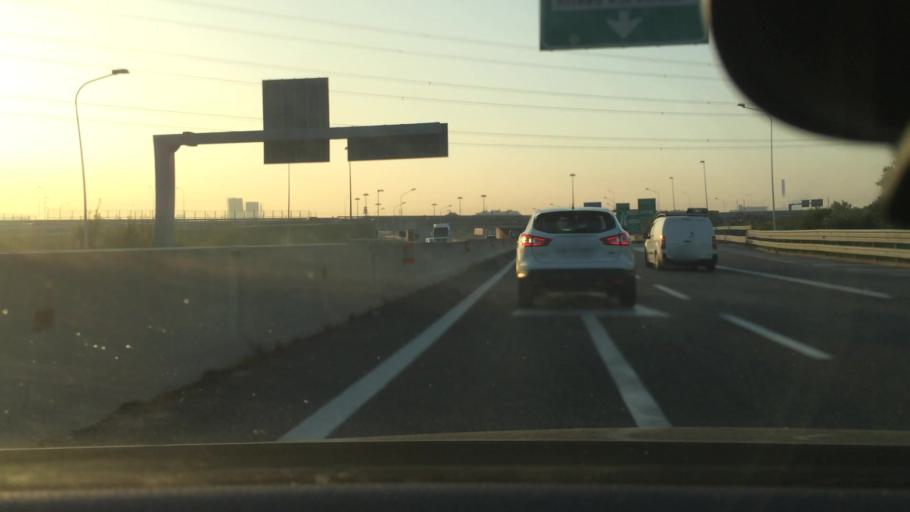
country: IT
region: Lombardy
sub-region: Citta metropolitana di Milano
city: Rho
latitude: 45.5265
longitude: 9.0582
